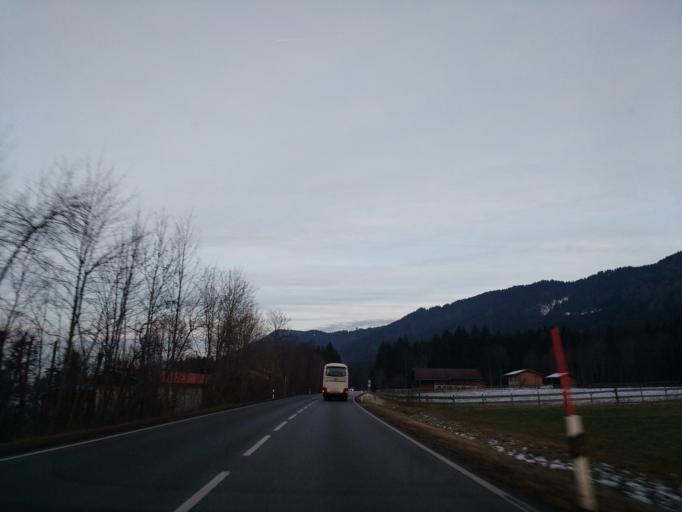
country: DE
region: Bavaria
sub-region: Swabia
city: Schwangau
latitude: 47.5909
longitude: 10.7702
